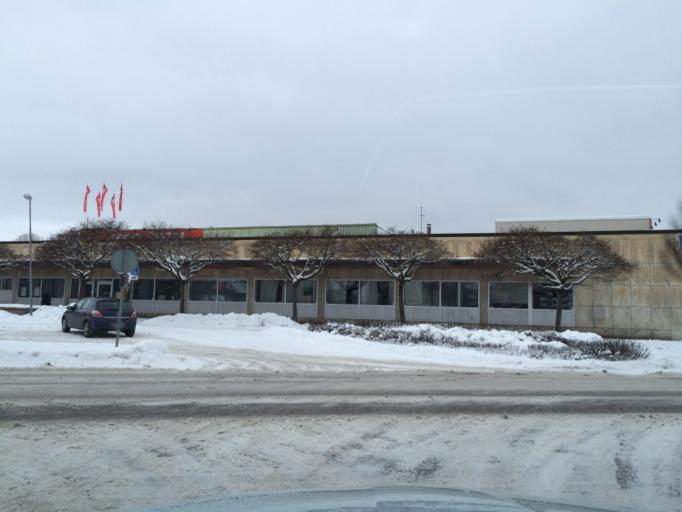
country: SE
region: Vaestmanland
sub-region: Hallstahammars Kommun
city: Hallstahammar
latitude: 59.6131
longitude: 16.2315
